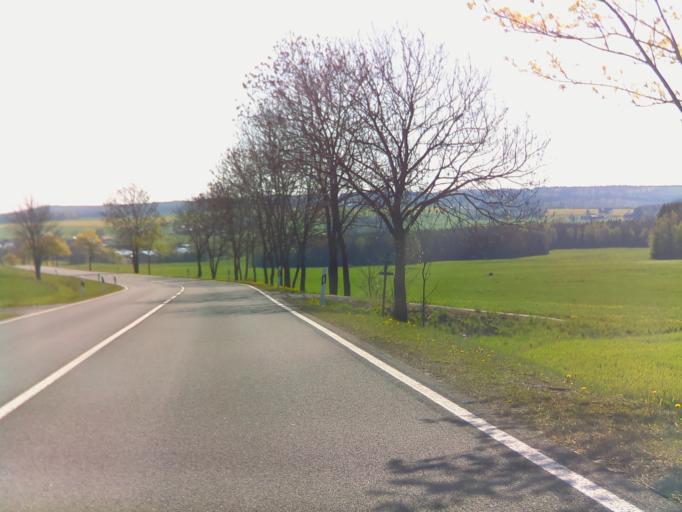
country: DE
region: Saxony
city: Pausa
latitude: 50.5468
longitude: 11.9959
